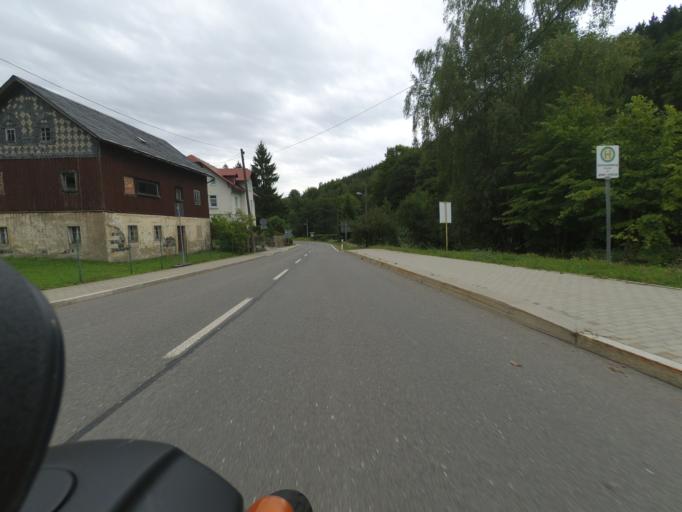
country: DE
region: Saxony
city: Schmiedeberg
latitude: 50.8279
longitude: 13.6660
